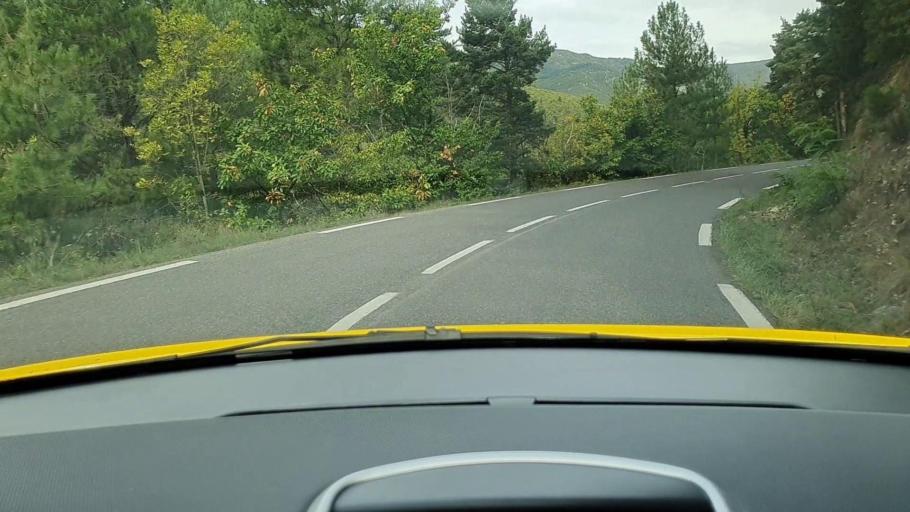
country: FR
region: Languedoc-Roussillon
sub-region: Departement du Gard
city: Le Vigan
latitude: 44.0112
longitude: 3.5944
